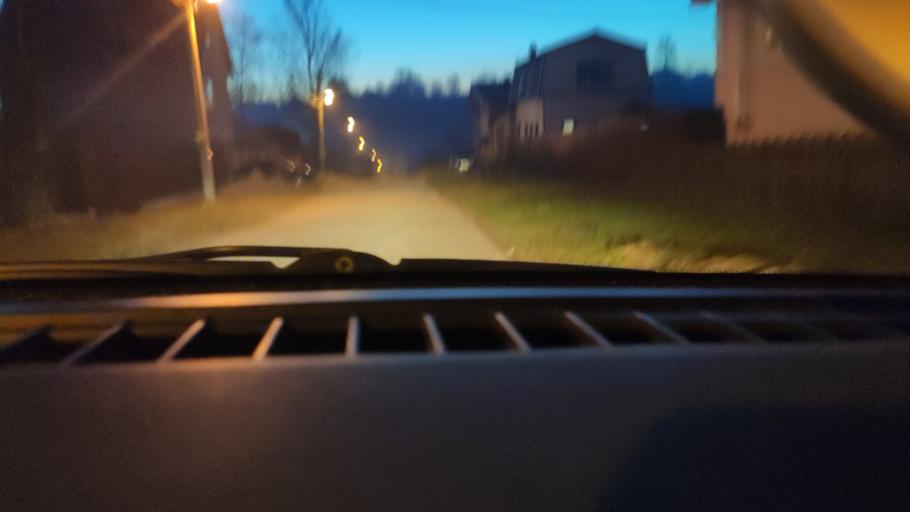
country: RU
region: Perm
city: Perm
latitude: 58.0413
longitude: 56.3336
